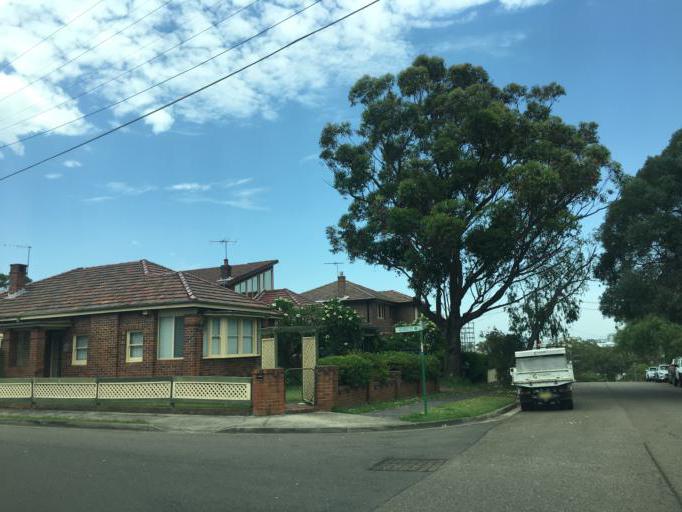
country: AU
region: New South Wales
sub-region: Hunters Hill
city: Gladesville
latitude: -33.8328
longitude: 151.1223
